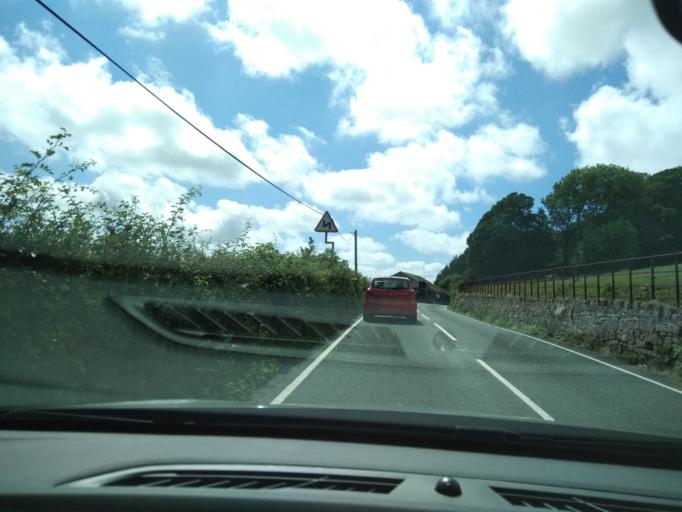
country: GB
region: England
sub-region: Cumbria
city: Millom
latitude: 54.2450
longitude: -3.3127
